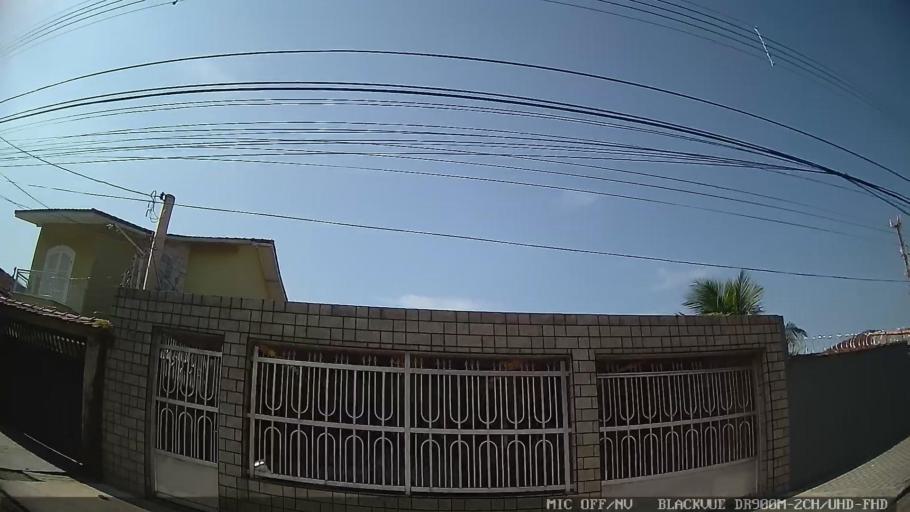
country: BR
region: Sao Paulo
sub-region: Guaruja
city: Guaruja
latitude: -23.9851
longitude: -46.2696
